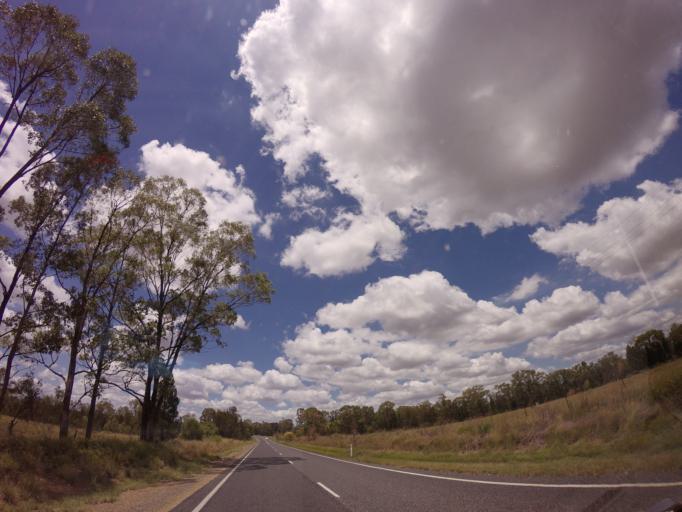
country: AU
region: Queensland
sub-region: Western Downs
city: Dalby
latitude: -27.9726
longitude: 151.1080
